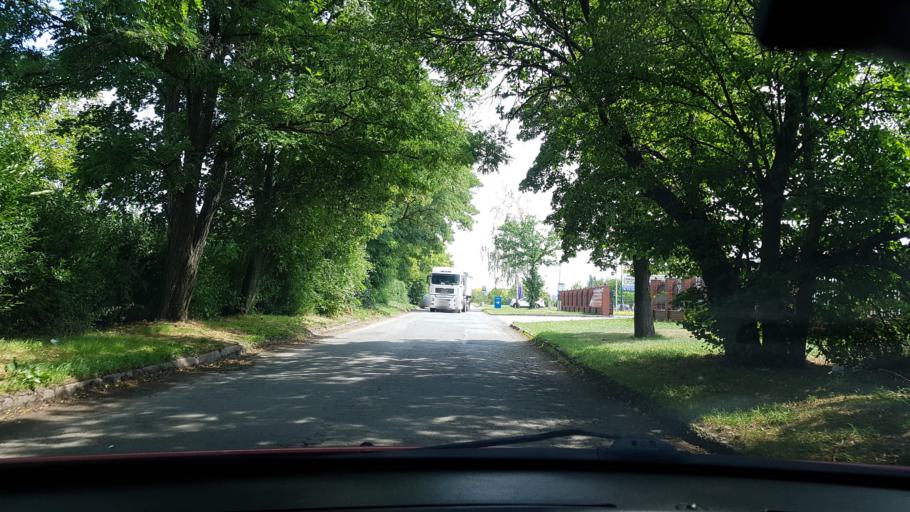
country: PL
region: Lower Silesian Voivodeship
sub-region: Powiat zabkowicki
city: Zabkowice Slaskie
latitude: 50.6033
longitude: 16.8184
